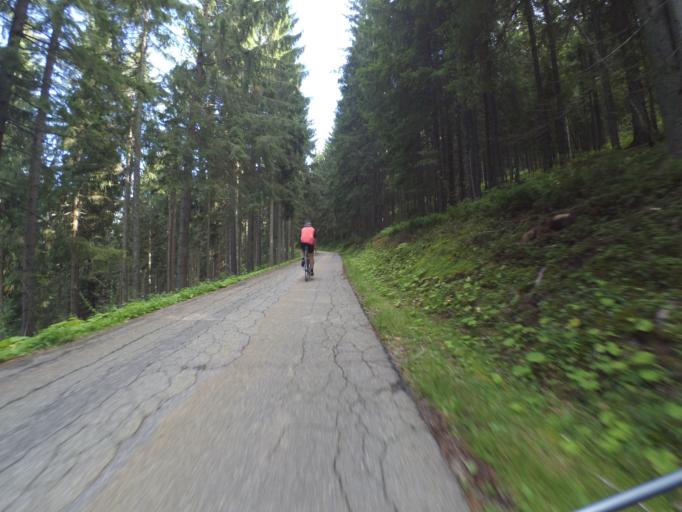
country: DE
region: Baden-Wuerttemberg
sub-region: Freiburg Region
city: Titisee-Neustadt
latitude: 47.9061
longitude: 8.1887
